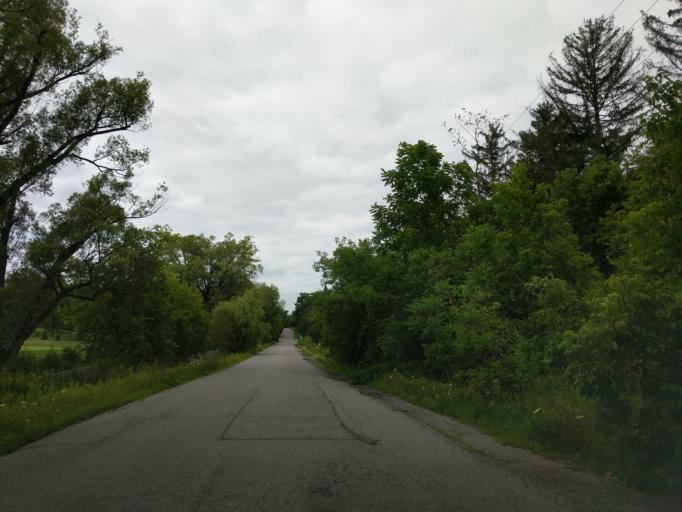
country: CA
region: Ontario
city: Willowdale
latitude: 43.8103
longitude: -79.3736
